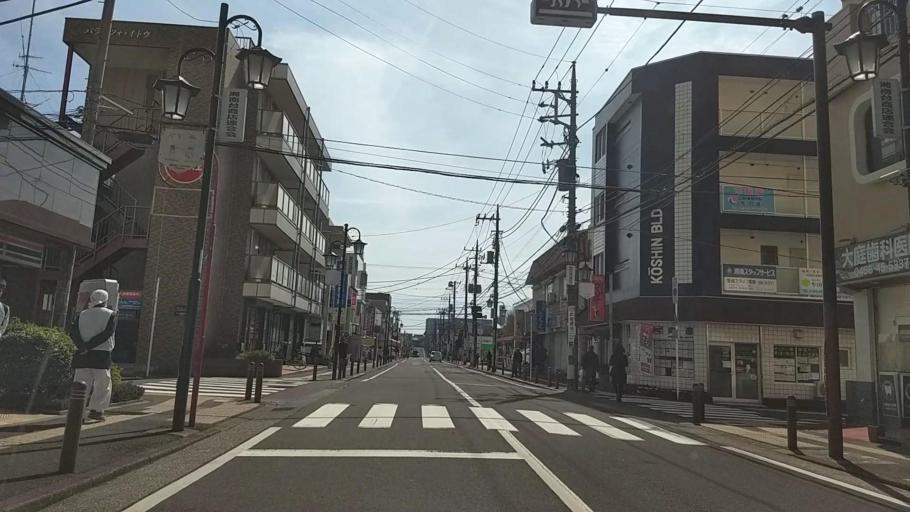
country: JP
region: Kanagawa
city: Fujisawa
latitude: 35.3953
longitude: 139.4654
